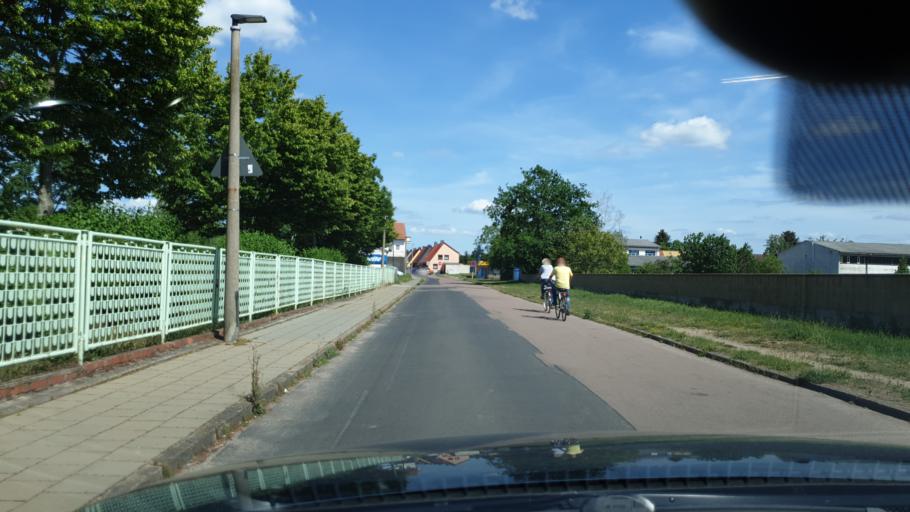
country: DE
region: Saxony-Anhalt
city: Dessau
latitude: 51.8053
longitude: 12.2526
